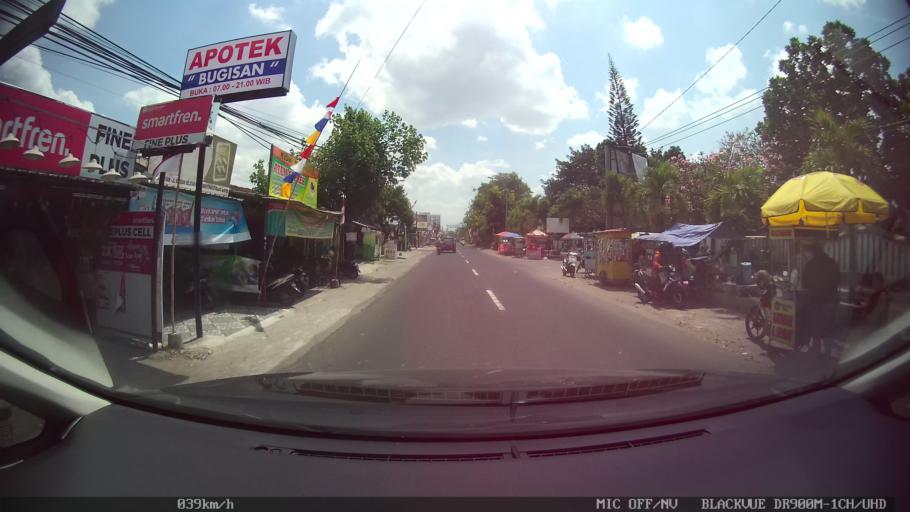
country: ID
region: Daerah Istimewa Yogyakarta
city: Kasihan
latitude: -7.8153
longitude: 110.3488
